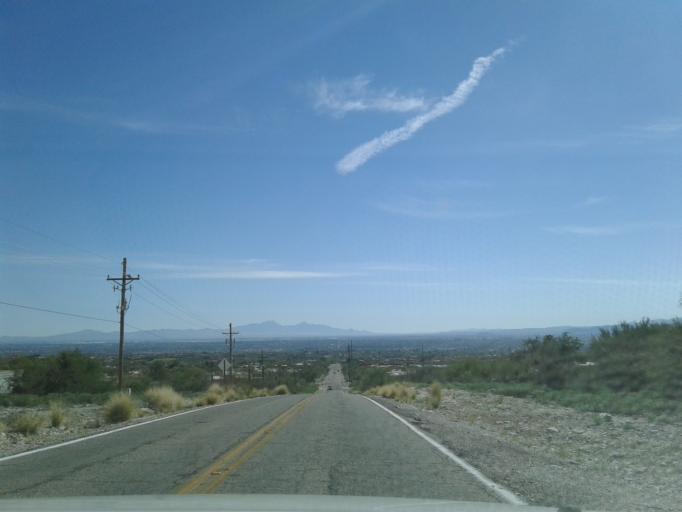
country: US
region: Arizona
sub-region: Pima County
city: Catalina Foothills
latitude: 32.3363
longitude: -110.9271
